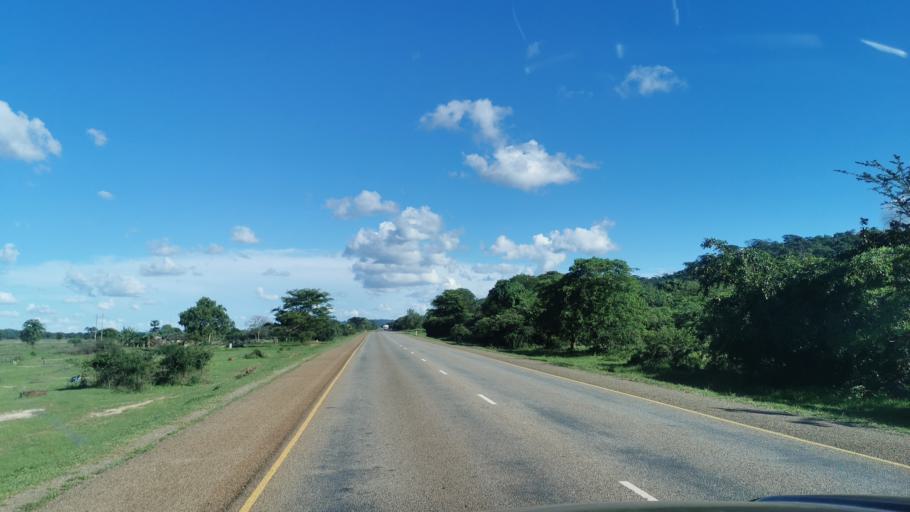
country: TZ
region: Geita
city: Masumbwe
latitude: -3.7183
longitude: 32.2930
